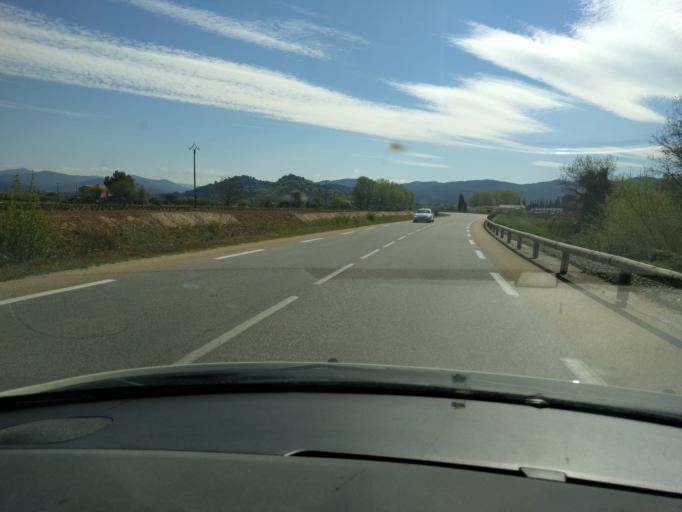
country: FR
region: Provence-Alpes-Cote d'Azur
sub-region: Departement du Var
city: Pierrefeu-du-Var
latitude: 43.2273
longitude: 6.1205
